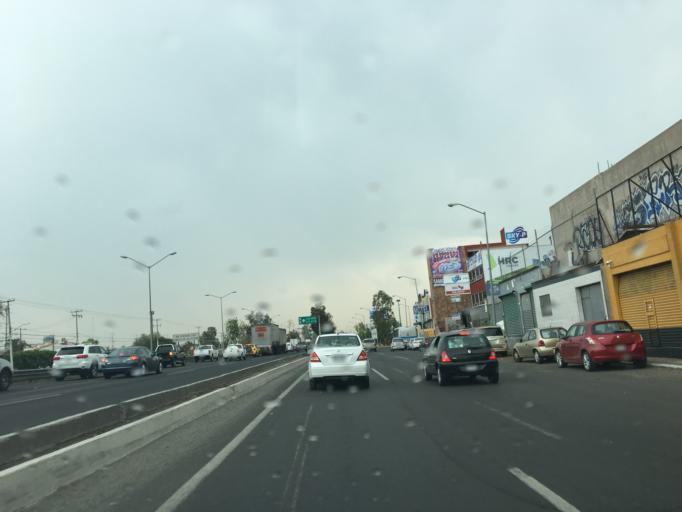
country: MX
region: Queretaro
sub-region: Queretaro
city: Santiago de Queretaro
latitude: 20.5785
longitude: -100.3797
